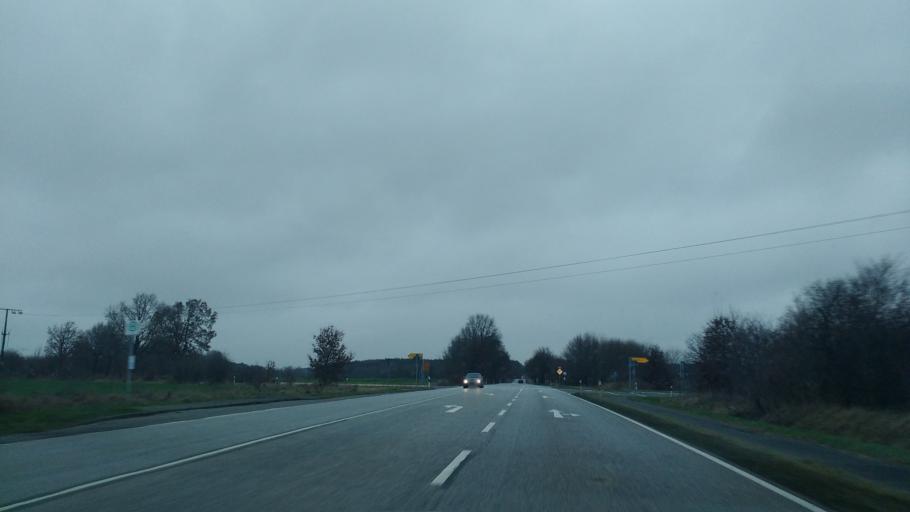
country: DE
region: Schleswig-Holstein
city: Silzen
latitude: 54.0328
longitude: 9.6033
